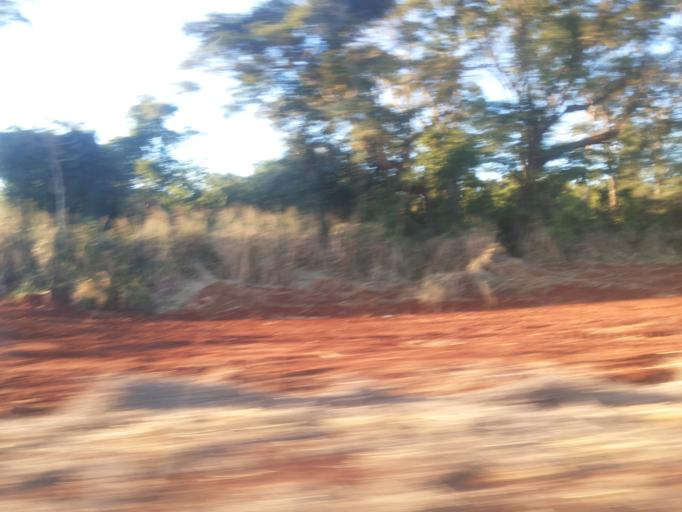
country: BR
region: Minas Gerais
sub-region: Centralina
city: Centralina
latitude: -18.7249
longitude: -49.2756
